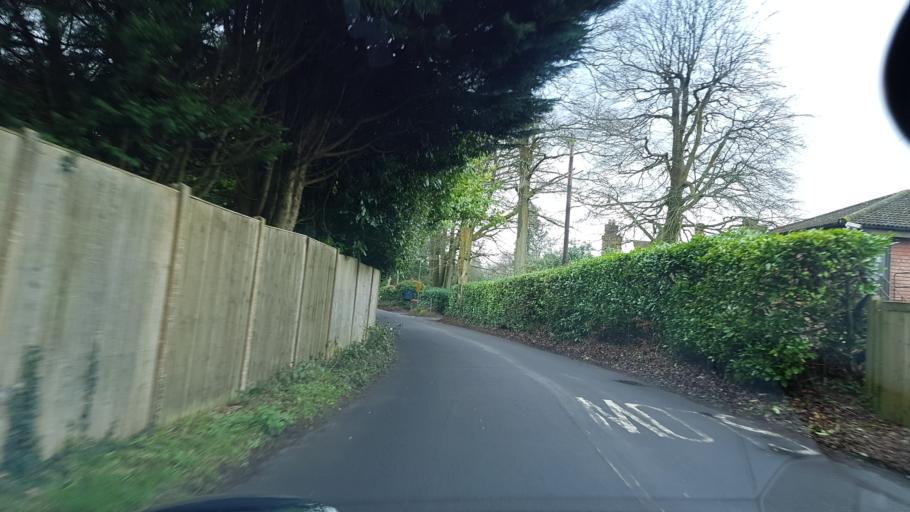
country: GB
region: England
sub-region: Surrey
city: Hindhead
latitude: 51.1049
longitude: -0.7416
